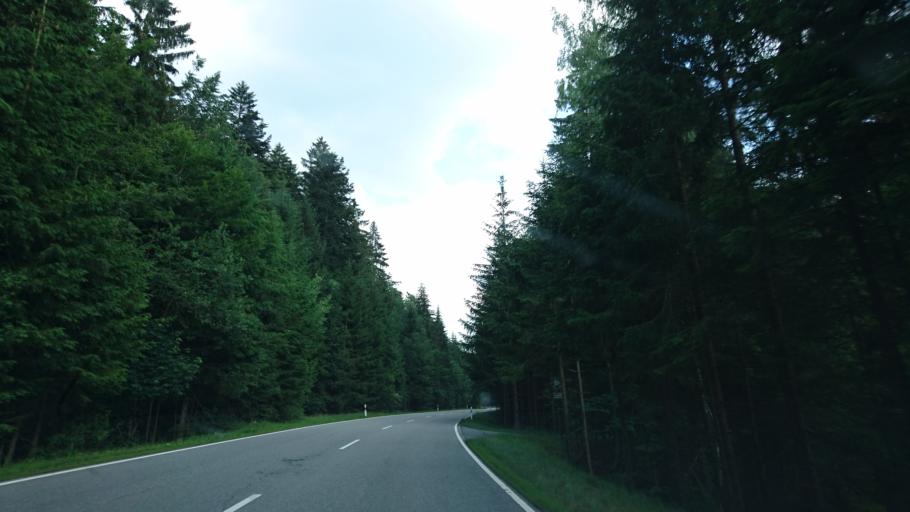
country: DE
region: Bavaria
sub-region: Lower Bavaria
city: Spiegelau
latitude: 48.9228
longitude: 13.4195
